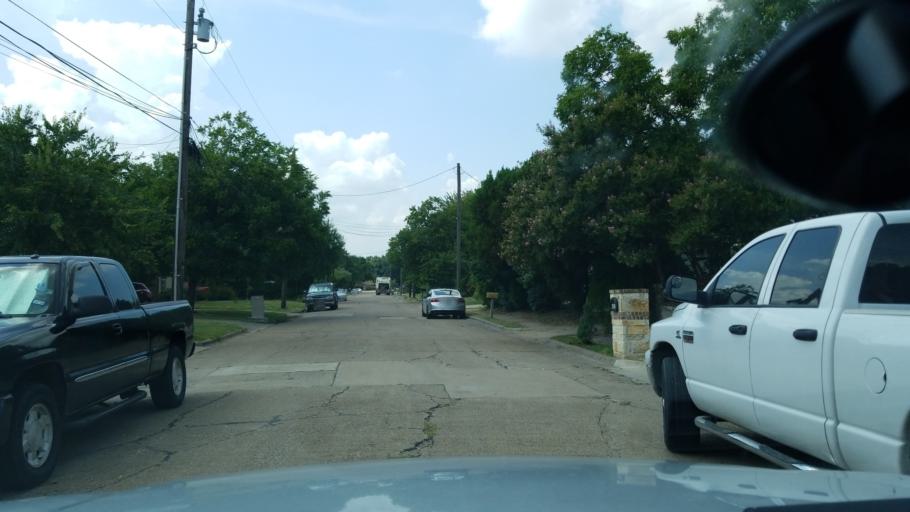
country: US
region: Texas
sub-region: Dallas County
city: Irving
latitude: 32.8333
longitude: -96.9204
